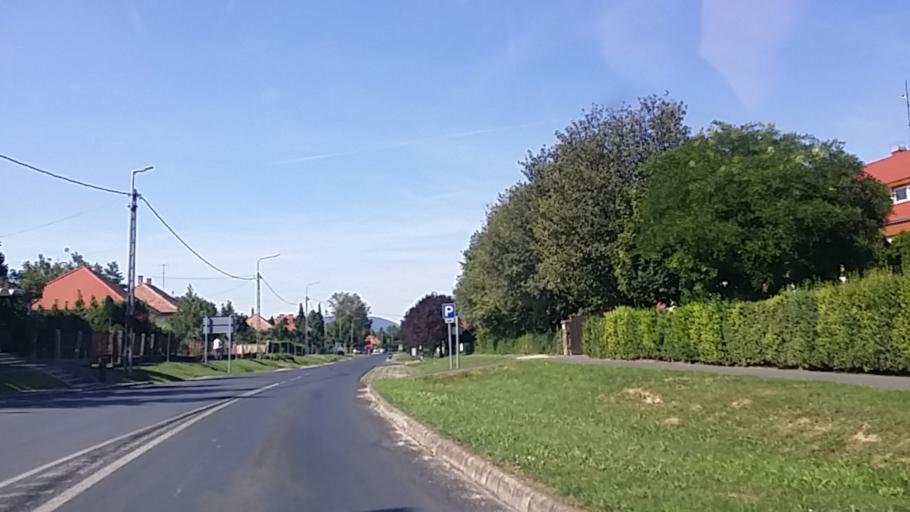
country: HU
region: Somogy
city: Balatonbereny
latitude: 46.6981
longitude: 17.3701
